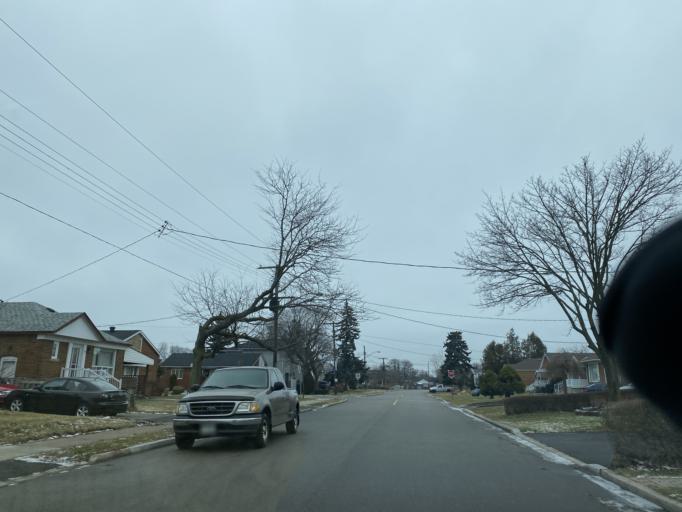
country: CA
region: Ontario
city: Scarborough
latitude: 43.7619
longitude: -79.3092
